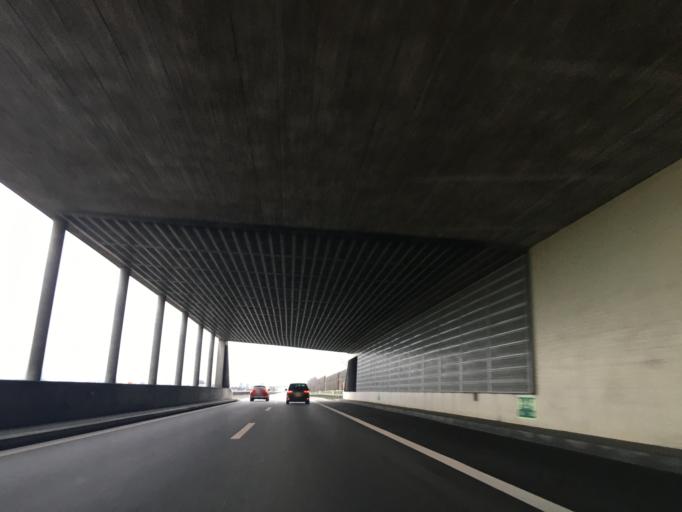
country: CH
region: Bern
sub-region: Seeland District
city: Leuzigen
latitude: 47.1793
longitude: 7.4517
